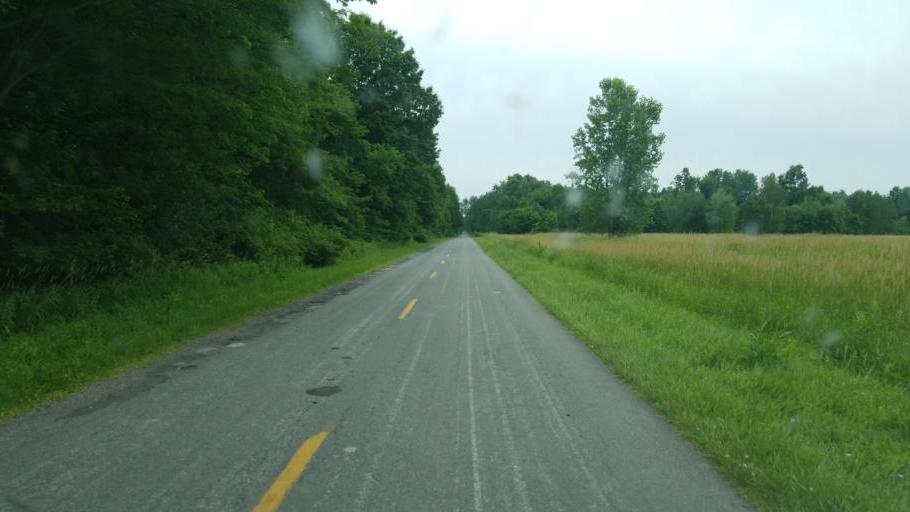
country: US
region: Ohio
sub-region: Trumbull County
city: Cortland
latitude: 41.4220
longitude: -80.7769
